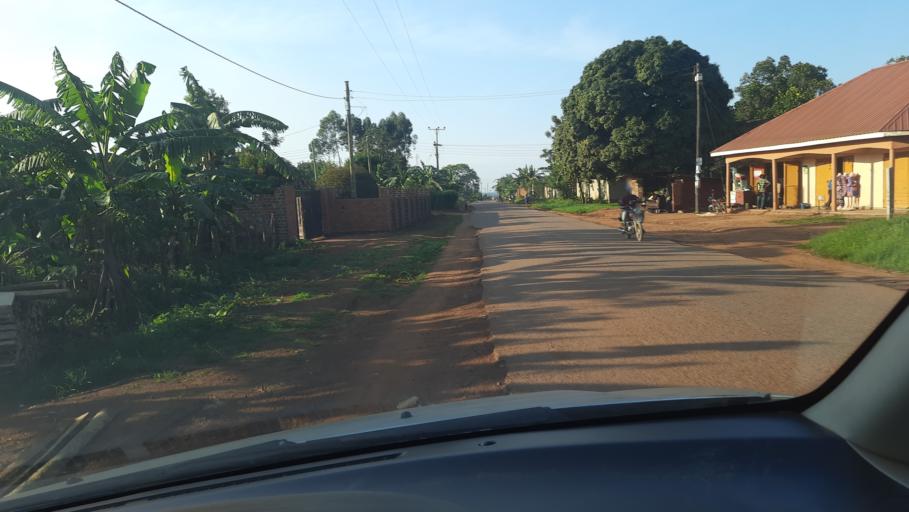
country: UG
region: Central Region
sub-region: Mukono District
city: Mukono
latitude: 0.3772
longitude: 32.7463
